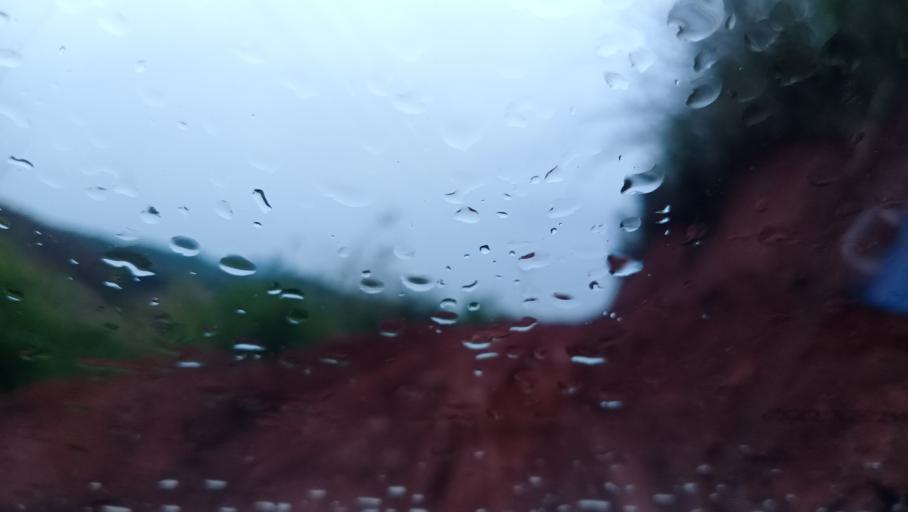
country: CN
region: Yunnan
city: Menglie
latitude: 22.2218
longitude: 101.6458
